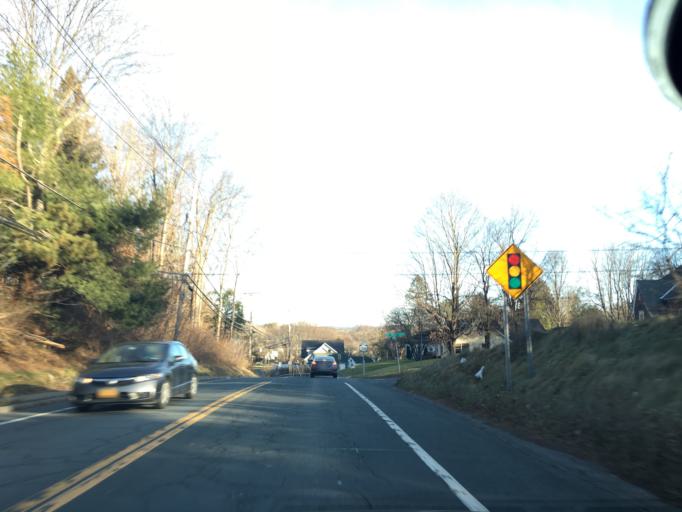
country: US
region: New York
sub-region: Rensselaer County
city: Wynantskill
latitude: 42.6902
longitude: -73.6400
